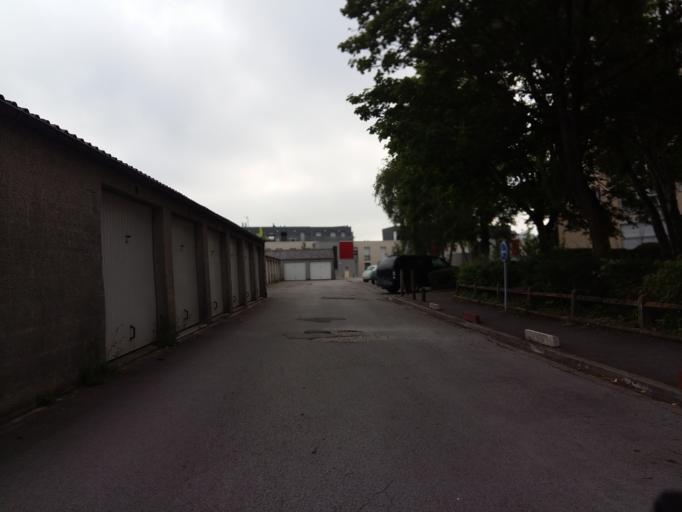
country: FR
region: Picardie
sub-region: Departement de la Somme
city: Amiens
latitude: 49.9104
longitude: 2.2913
